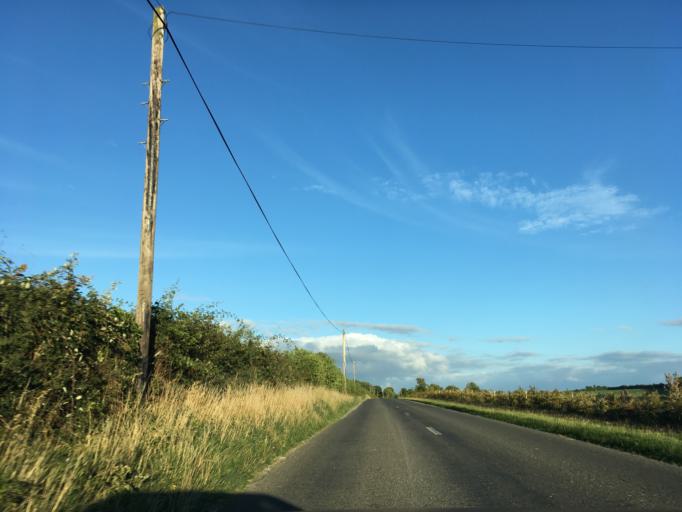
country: IE
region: Munster
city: Cashel
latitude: 52.4859
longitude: -7.9458
